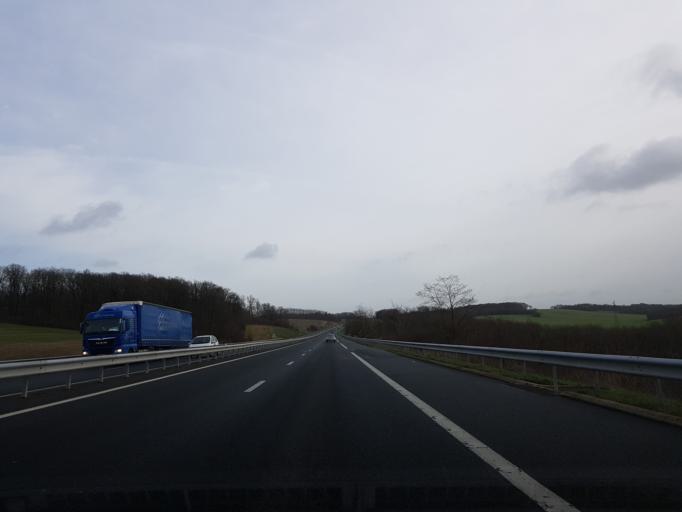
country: FR
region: Bourgogne
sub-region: Departement de l'Yonne
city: Thorigny-sur-Oreuse
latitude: 48.2351
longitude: 3.3995
